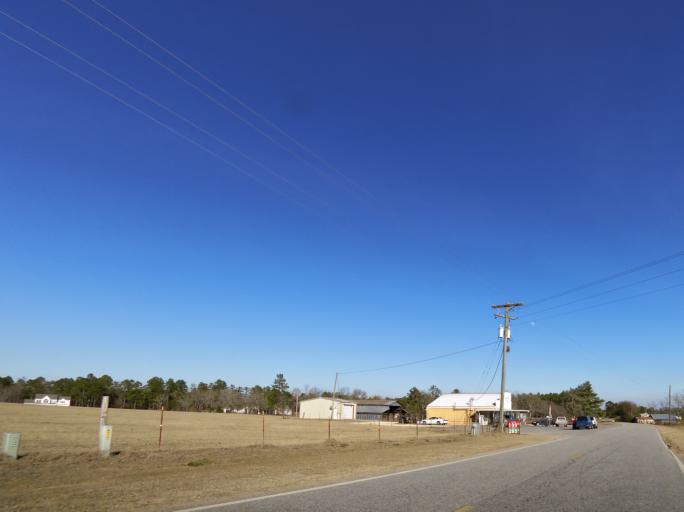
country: US
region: Georgia
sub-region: Bibb County
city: West Point
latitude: 32.7558
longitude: -83.8927
